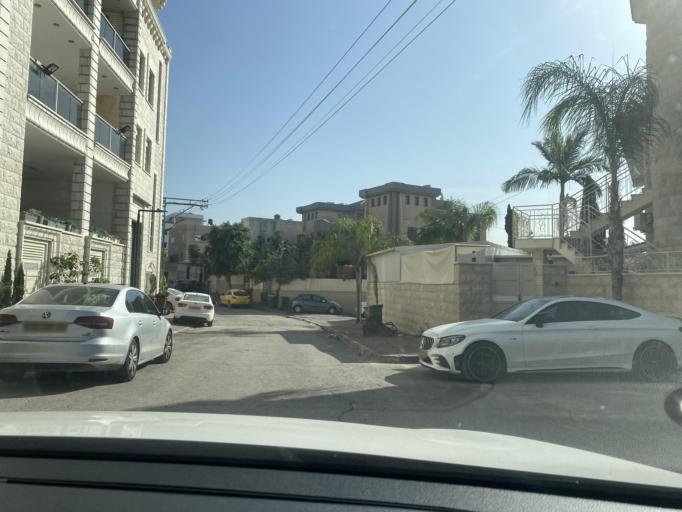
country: IL
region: Central District
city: Kafr Qasim
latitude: 32.1308
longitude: 34.9707
